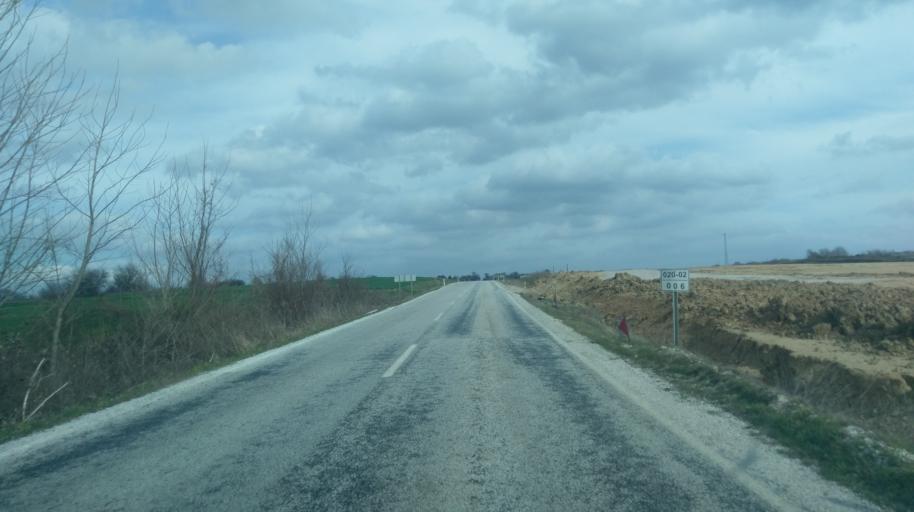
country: TR
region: Kirklareli
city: Inece
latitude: 41.6685
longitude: 26.9710
